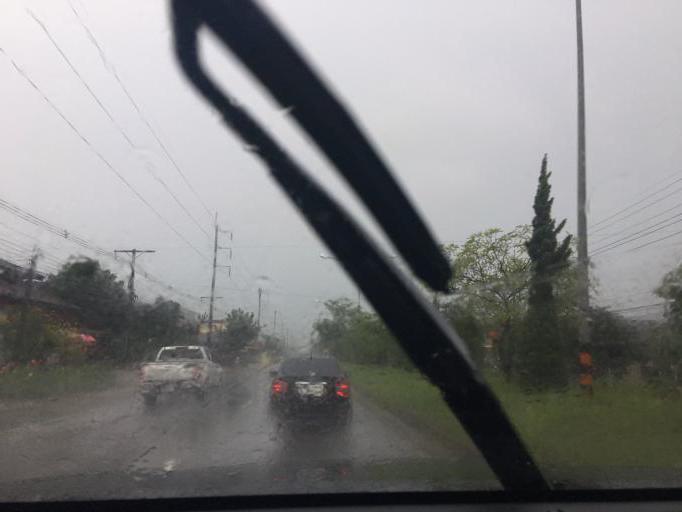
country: TH
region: Chiang Rai
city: Mae Fa Luang
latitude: 20.2455
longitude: 99.8561
